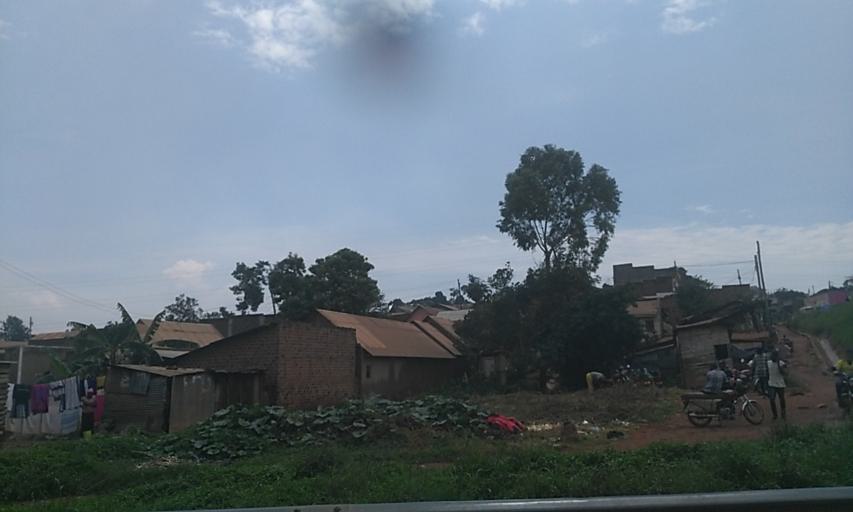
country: UG
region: Central Region
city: Kampala Central Division
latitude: 0.3472
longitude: 32.5538
